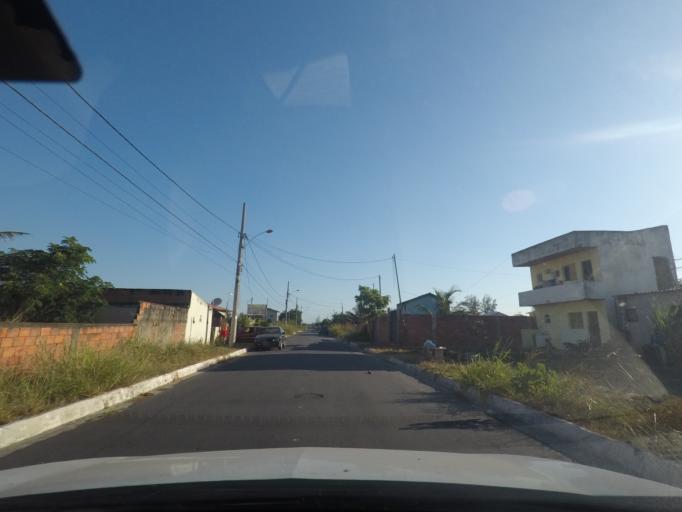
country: BR
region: Rio de Janeiro
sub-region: Marica
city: Marica
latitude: -22.9568
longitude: -42.9380
